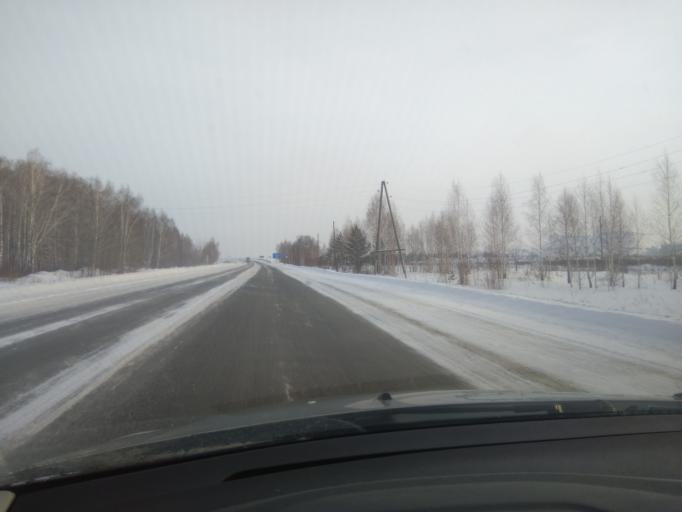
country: RU
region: Sverdlovsk
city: Bogdanovich
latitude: 56.8079
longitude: 62.0344
